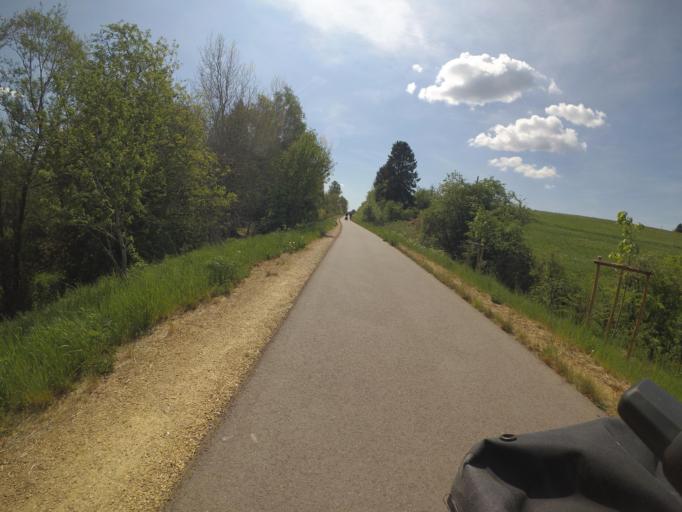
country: BE
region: Wallonia
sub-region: Province de Liege
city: Bullange
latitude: 50.4162
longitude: 6.2563
